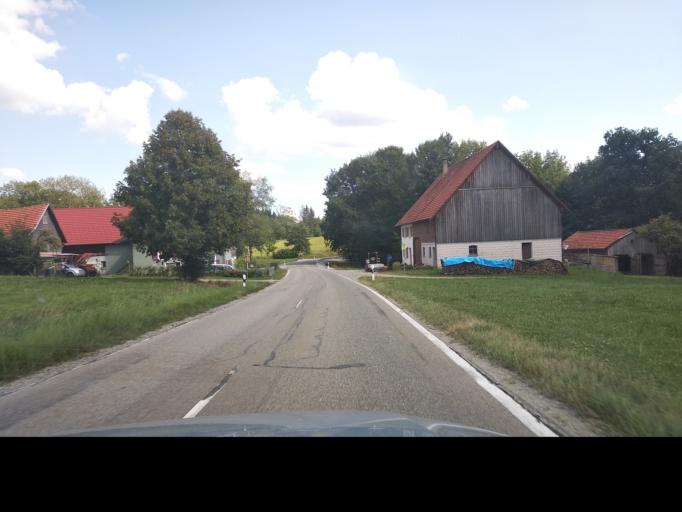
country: DE
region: Baden-Wuerttemberg
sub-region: Tuebingen Region
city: Leutkirch im Allgau
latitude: 47.8782
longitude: 9.9914
